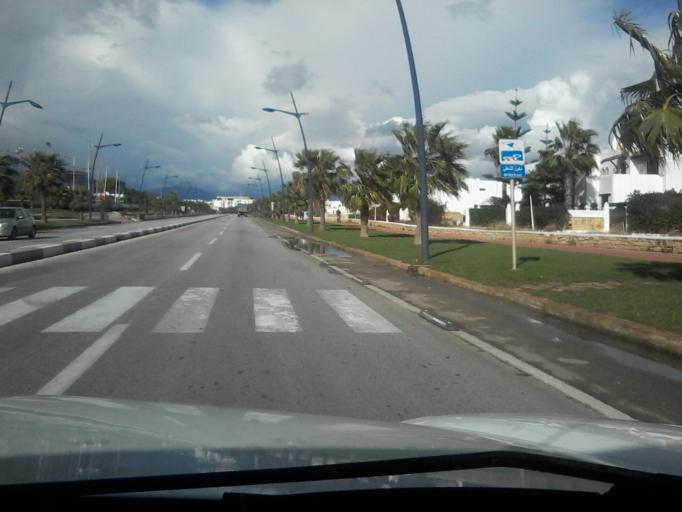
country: MA
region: Tanger-Tetouan
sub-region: Tetouan
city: Martil
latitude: 35.7402
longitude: -5.3432
